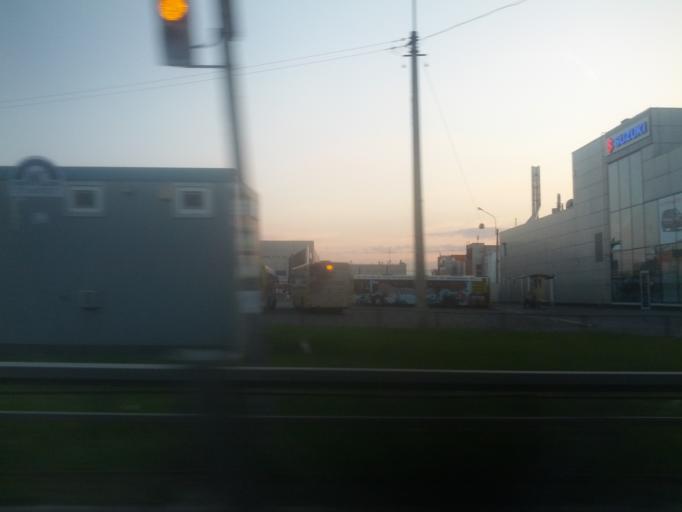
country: RU
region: St.-Petersburg
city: Staraya Derevnya
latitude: 59.9912
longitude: 30.2557
